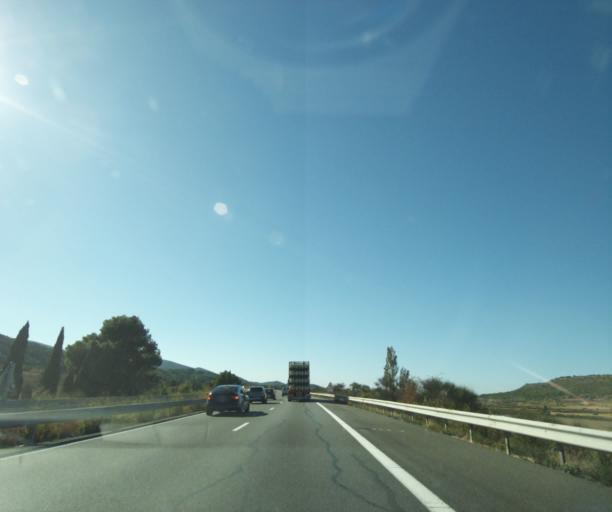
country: FR
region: Languedoc-Roussillon
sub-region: Departement de l'Aude
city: Fabrezan
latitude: 43.1730
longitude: 2.6917
